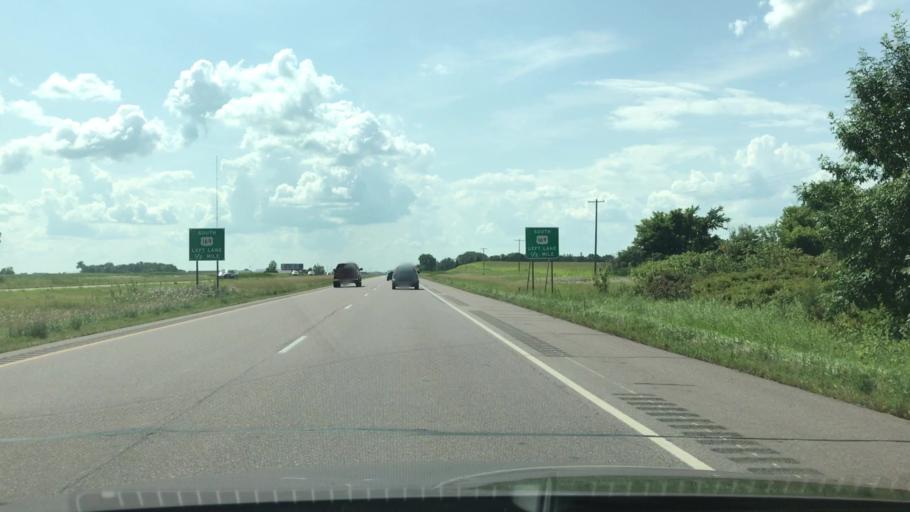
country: US
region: Minnesota
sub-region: Nicollet County
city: North Mankato
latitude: 44.1447
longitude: -94.1024
